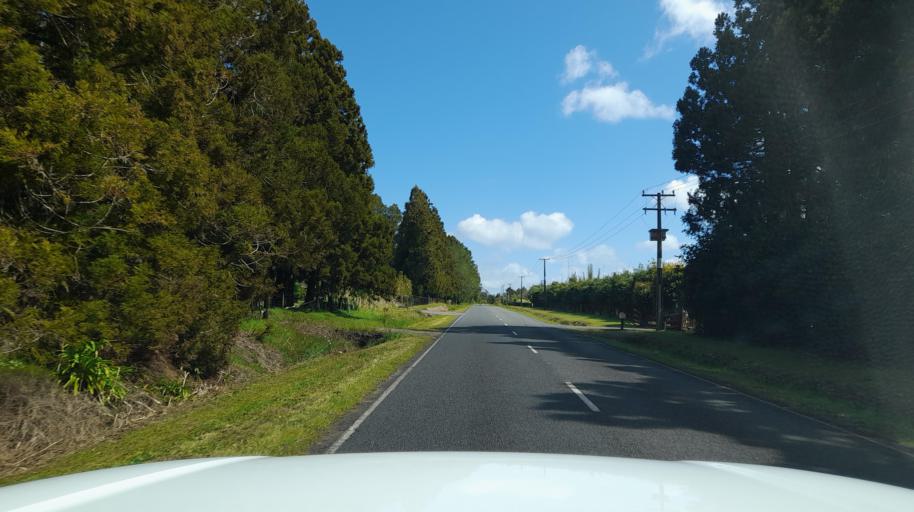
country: NZ
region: Northland
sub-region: Far North District
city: Kerikeri
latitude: -35.2408
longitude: 173.8913
